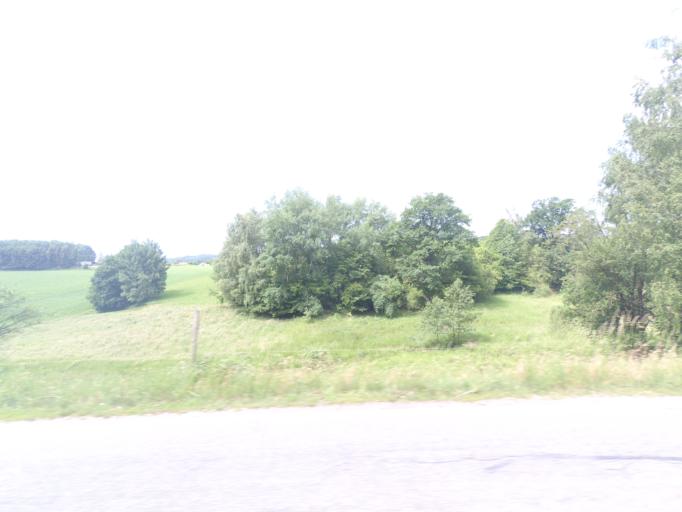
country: DE
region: Hesse
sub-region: Regierungsbezirk Darmstadt
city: Wald-Michelbach
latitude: 49.6250
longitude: 8.8396
